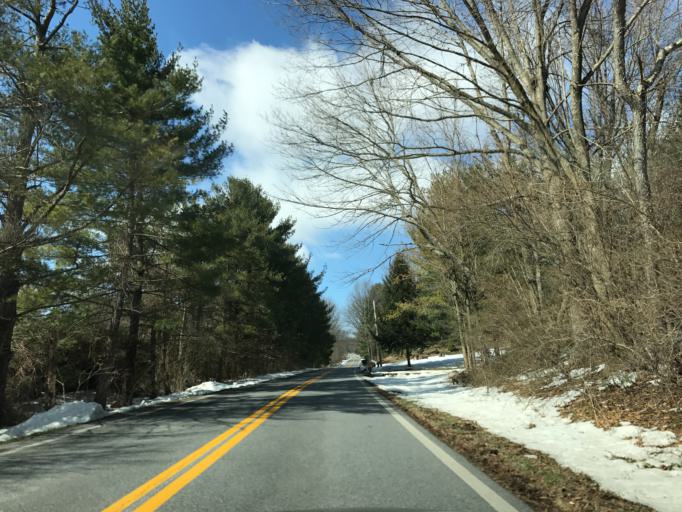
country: US
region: Maryland
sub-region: Carroll County
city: Hampstead
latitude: 39.6590
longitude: -76.8137
